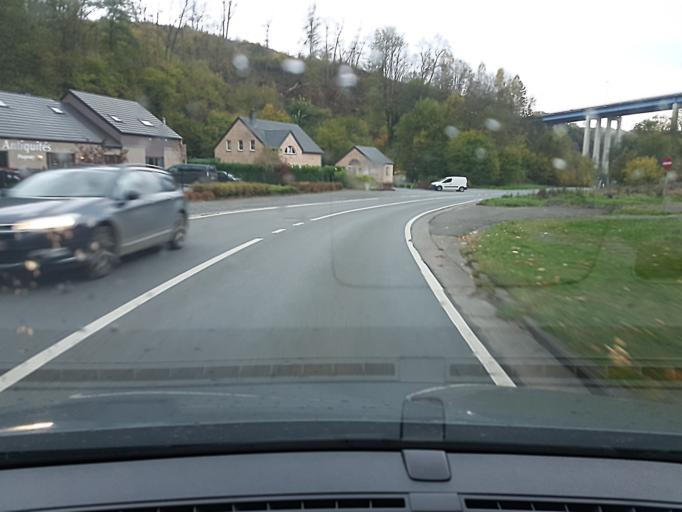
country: BE
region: Wallonia
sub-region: Province de Liege
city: Aywaille
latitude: 50.4860
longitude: 5.7198
